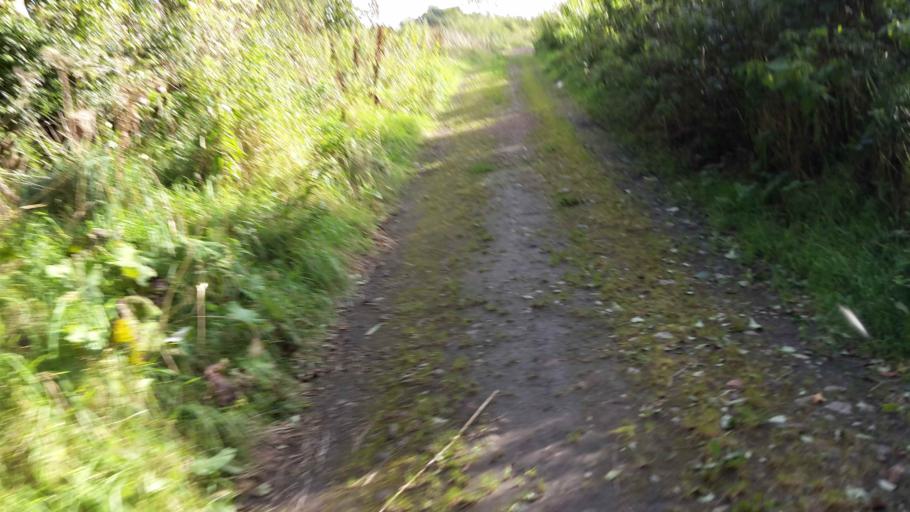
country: GB
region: Scotland
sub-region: South Lanarkshire
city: Carluke
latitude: 55.7204
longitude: -3.8278
